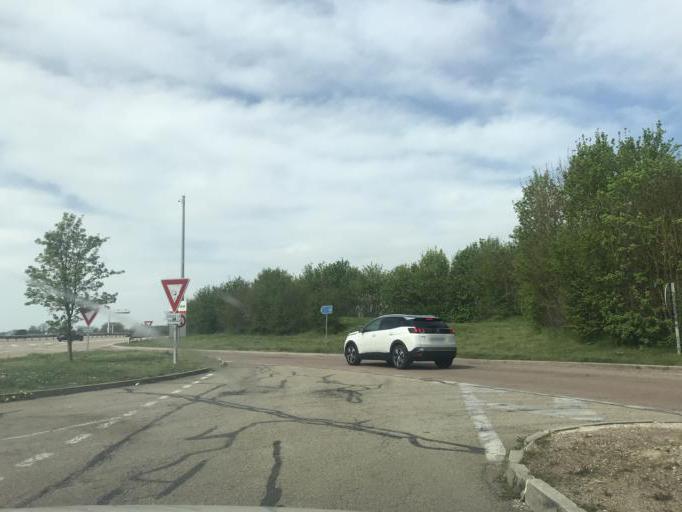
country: FR
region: Bourgogne
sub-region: Departement de l'Yonne
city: Avallon
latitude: 47.5040
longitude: 4.0330
